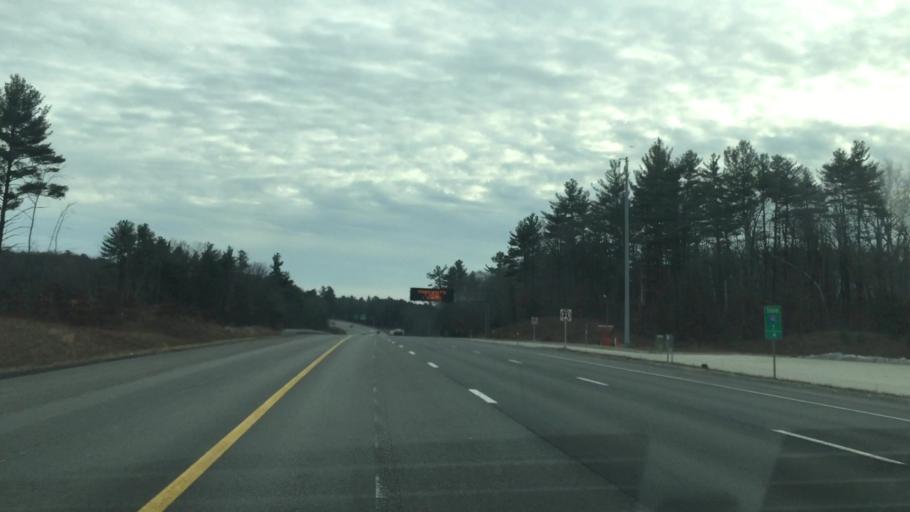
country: US
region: New Hampshire
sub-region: Rockingham County
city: Windham
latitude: 42.8229
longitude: -71.2898
